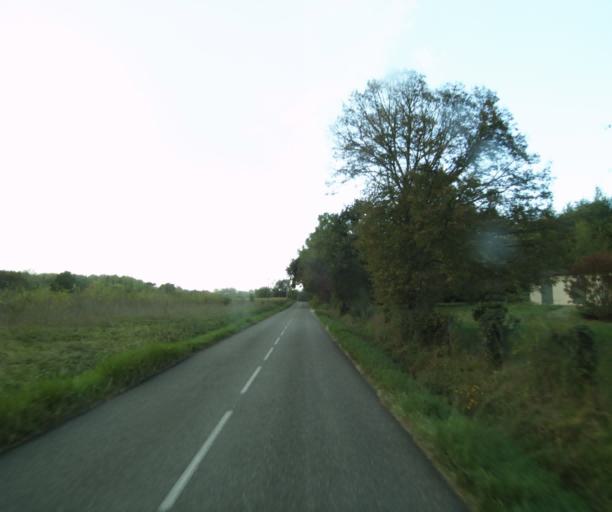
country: FR
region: Midi-Pyrenees
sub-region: Departement du Gers
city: Cazaubon
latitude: 43.9322
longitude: -0.0751
